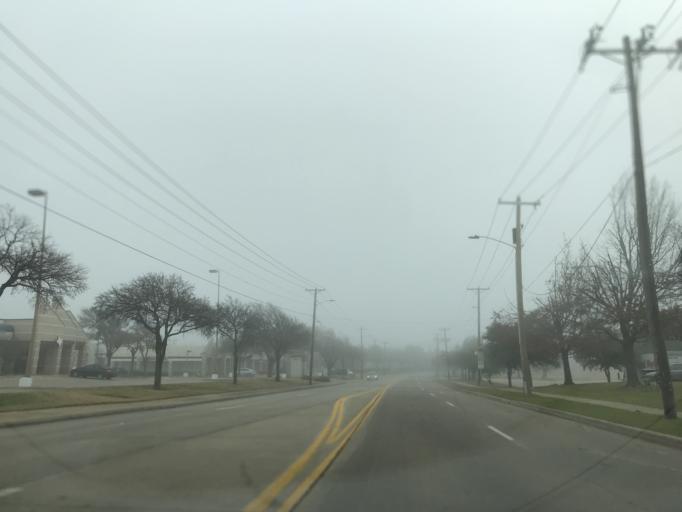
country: US
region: Texas
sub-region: Tarrant County
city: Arlington
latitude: 32.7734
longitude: -97.0824
